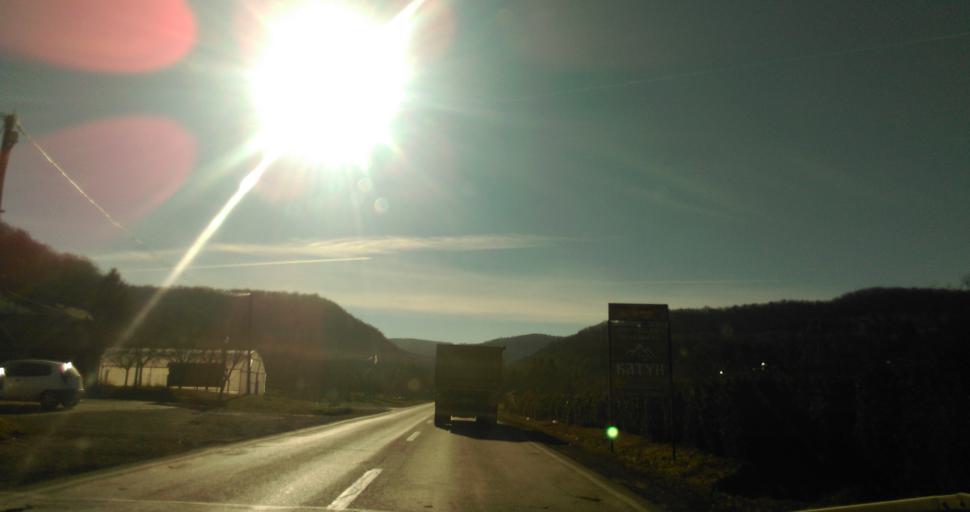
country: RS
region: Autonomna Pokrajina Vojvodina
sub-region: Juznobacki Okrug
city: Novi Sad
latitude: 45.1930
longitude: 19.8409
